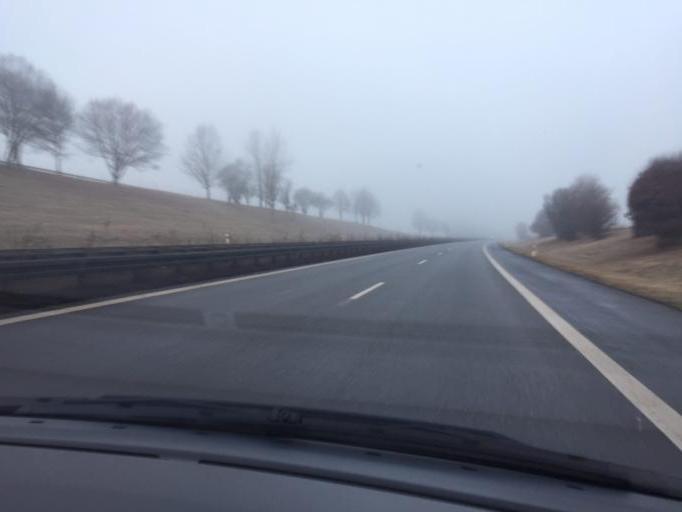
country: DE
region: Baden-Wuerttemberg
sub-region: Freiburg Region
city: Geisingen
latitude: 47.9341
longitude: 8.6279
